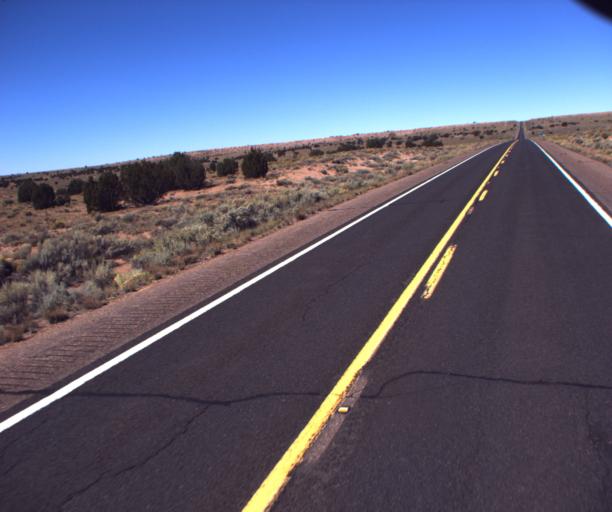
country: US
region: Arizona
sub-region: Navajo County
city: Snowflake
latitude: 34.6745
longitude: -109.7284
